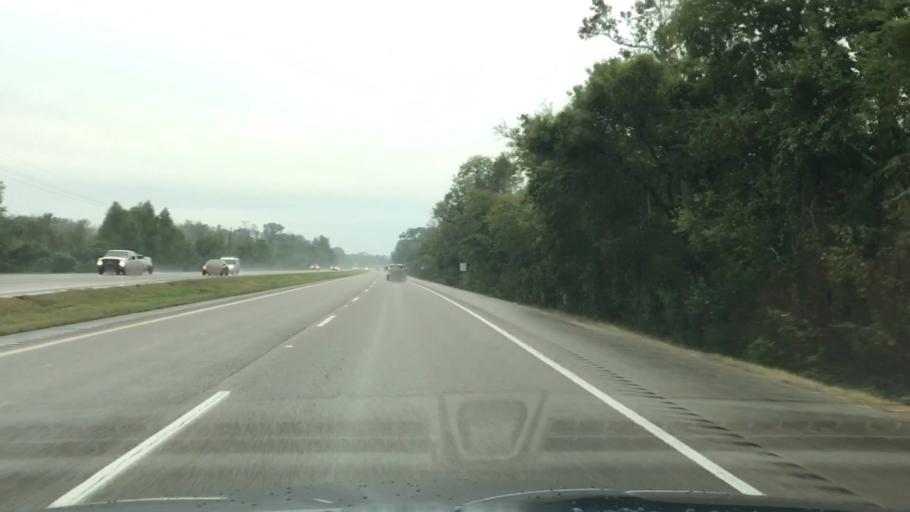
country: US
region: Louisiana
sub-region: Saint Charles Parish
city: Paradis
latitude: 29.8529
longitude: -90.4480
